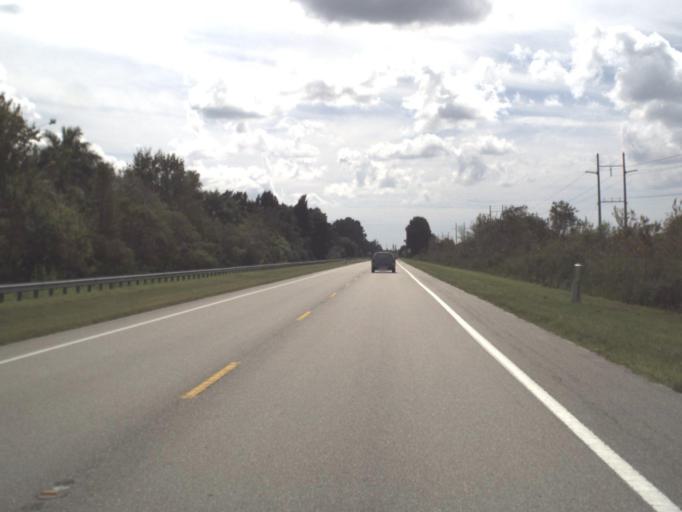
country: US
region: Florida
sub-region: Collier County
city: Lely Resort
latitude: 25.9607
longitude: -81.3547
